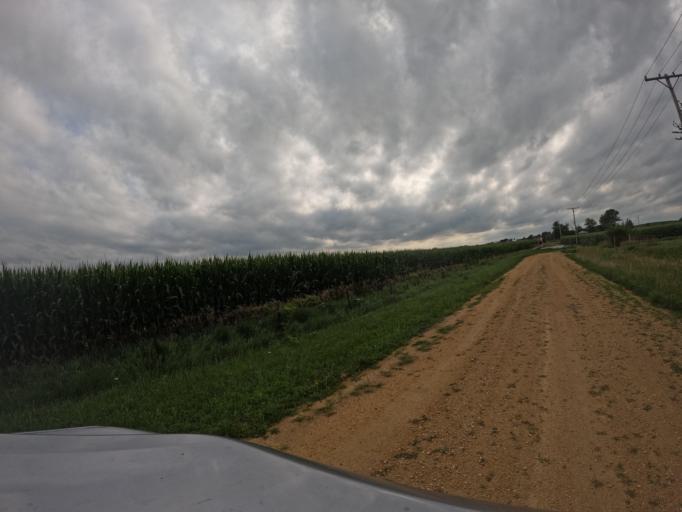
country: US
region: Iowa
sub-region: Clinton County
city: De Witt
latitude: 41.7967
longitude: -90.5652
